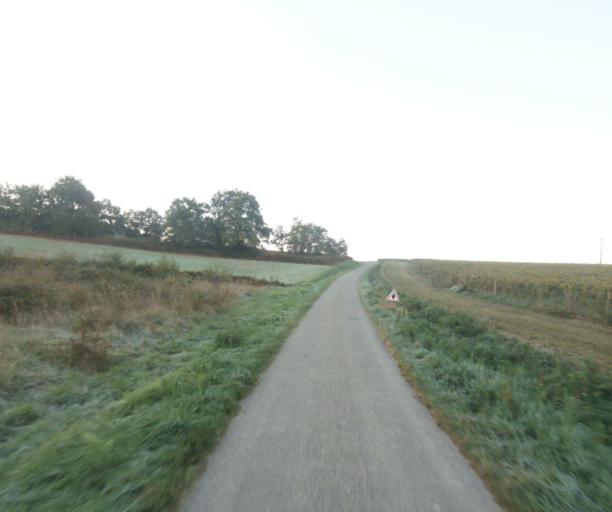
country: FR
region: Midi-Pyrenees
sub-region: Departement du Gers
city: Vic-Fezensac
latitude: 43.7860
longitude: 0.2375
